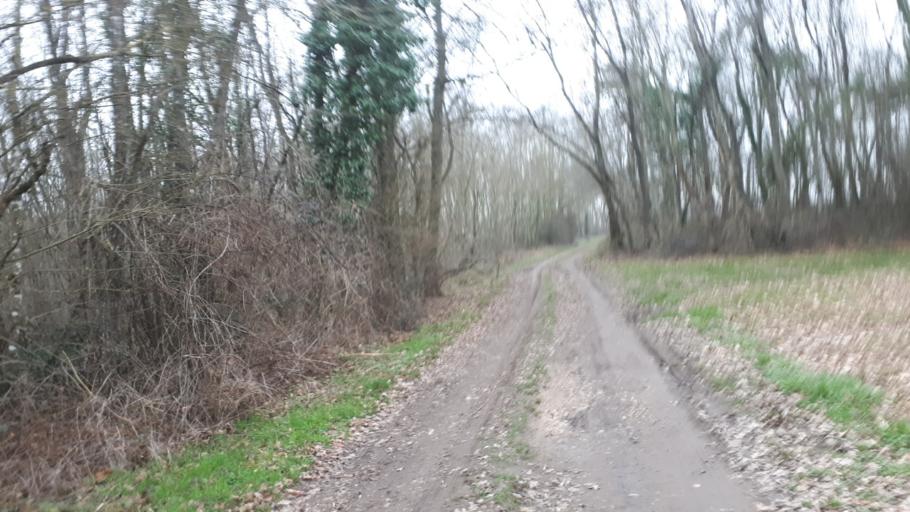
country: FR
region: Centre
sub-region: Departement du Loir-et-Cher
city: Villiers-sur-Loir
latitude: 47.8183
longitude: 1.0085
